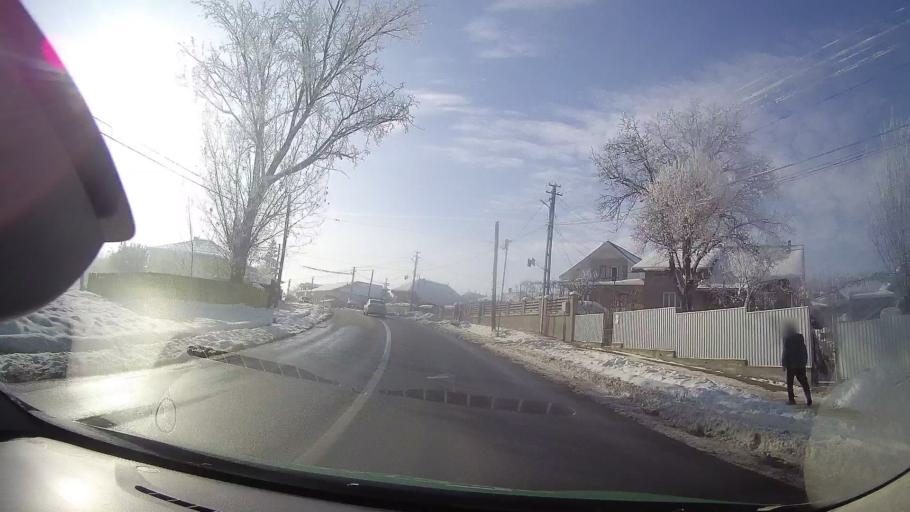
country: RO
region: Iasi
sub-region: Comuna Motca
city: Motca
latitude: 47.2390
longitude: 26.6042
